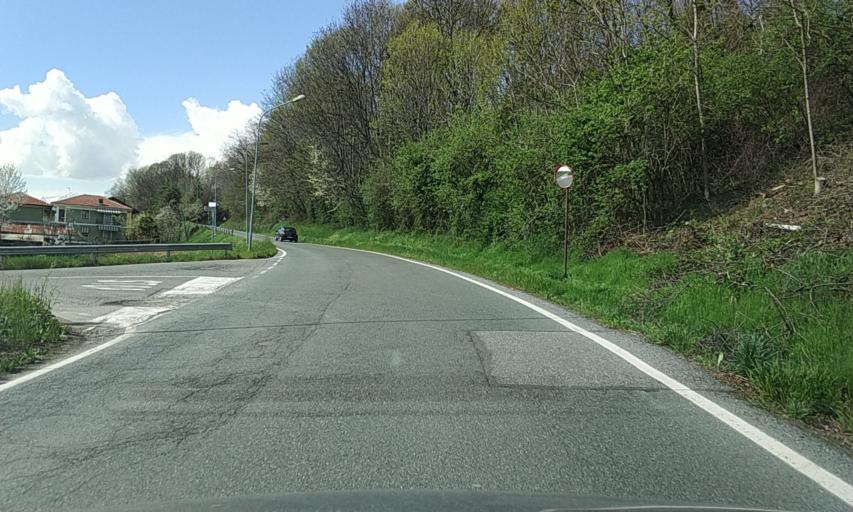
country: IT
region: Piedmont
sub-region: Provincia di Torino
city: San Carlo Canavese
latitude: 45.2466
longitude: 7.5991
